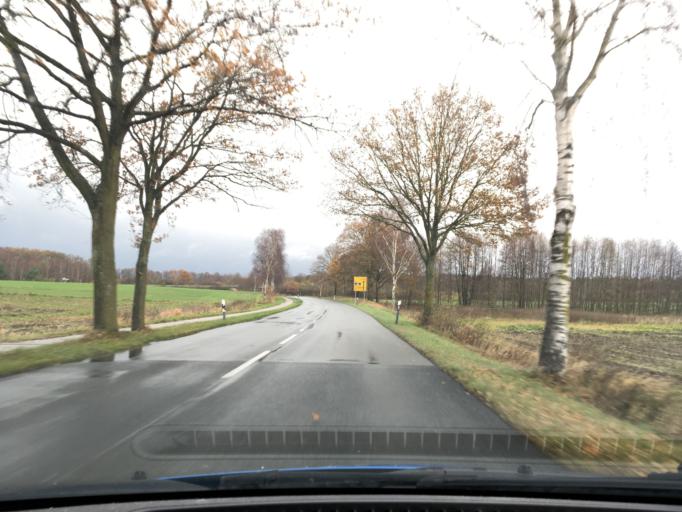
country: DE
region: Lower Saxony
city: Embsen
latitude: 53.1900
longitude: 10.3473
